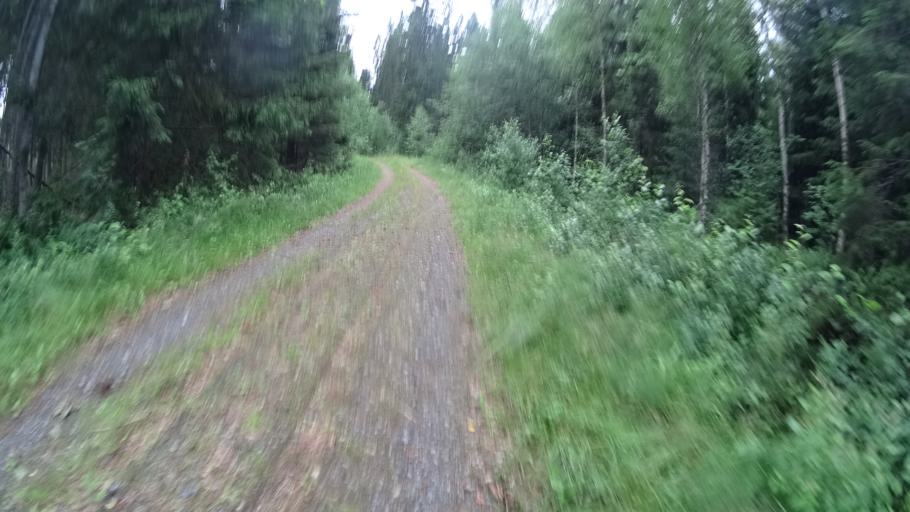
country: FI
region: Uusimaa
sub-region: Helsinki
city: Karkkila
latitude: 60.5672
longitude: 24.3347
